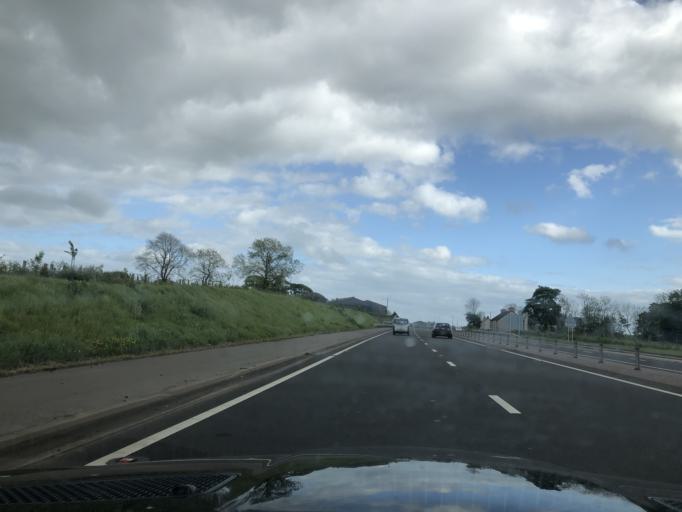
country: GB
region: Northern Ireland
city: Dunloy
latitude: 55.0101
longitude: -6.3626
